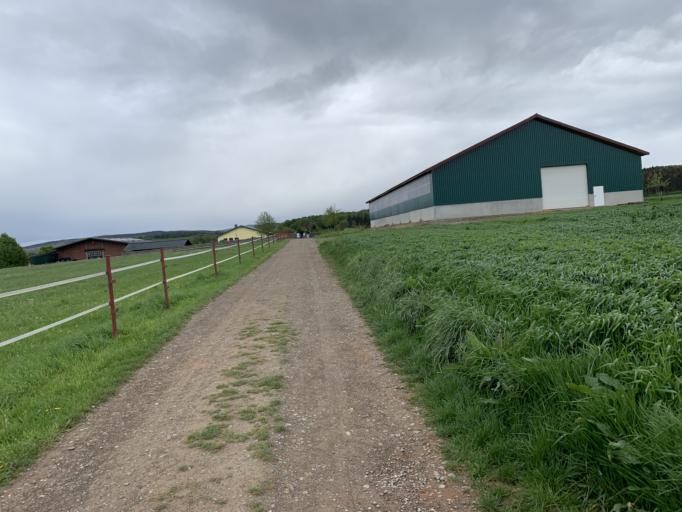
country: DE
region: North Rhine-Westphalia
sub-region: Regierungsbezirk Koln
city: Bad Munstereifel
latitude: 50.5954
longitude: 6.7330
